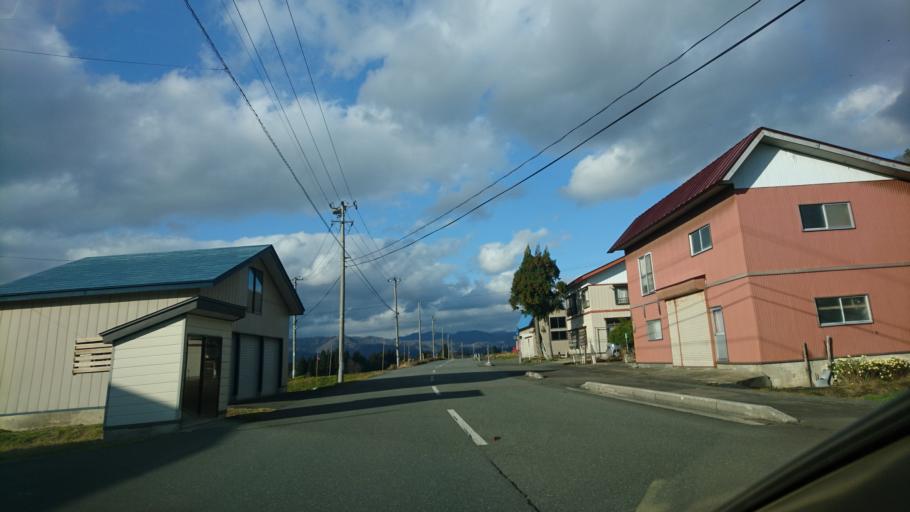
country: JP
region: Akita
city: Yokotemachi
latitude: 39.3767
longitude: 140.7670
